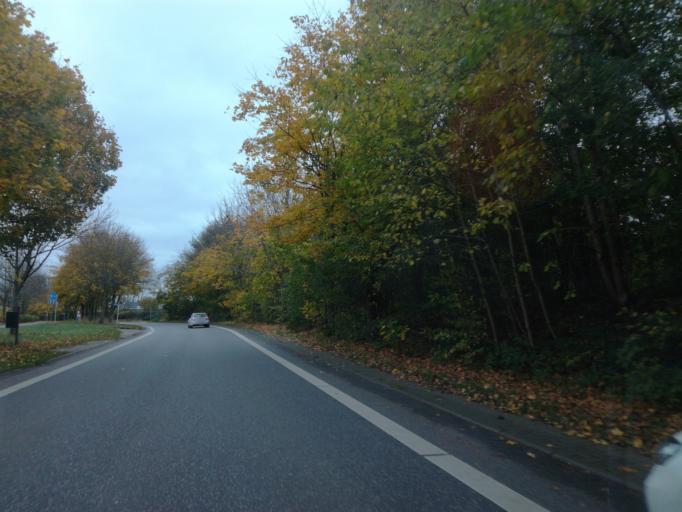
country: DK
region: South Denmark
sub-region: Fredericia Kommune
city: Snoghoj
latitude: 55.5491
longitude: 9.7066
